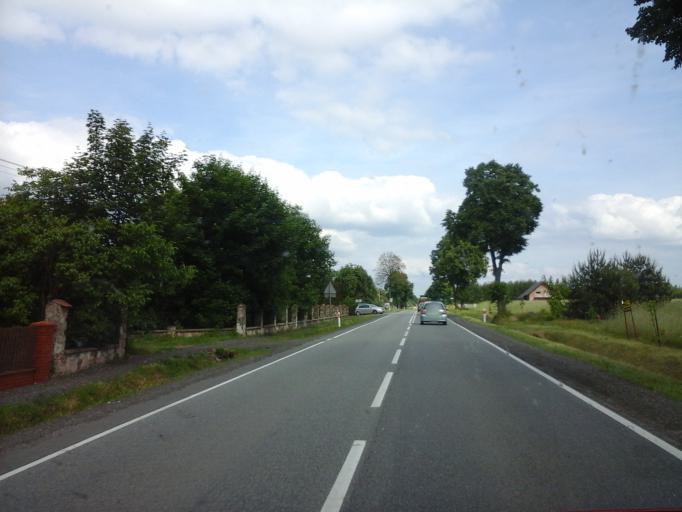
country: PL
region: Lodz Voivodeship
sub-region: Powiat opoczynski
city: Paradyz
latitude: 51.3087
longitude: 20.0983
